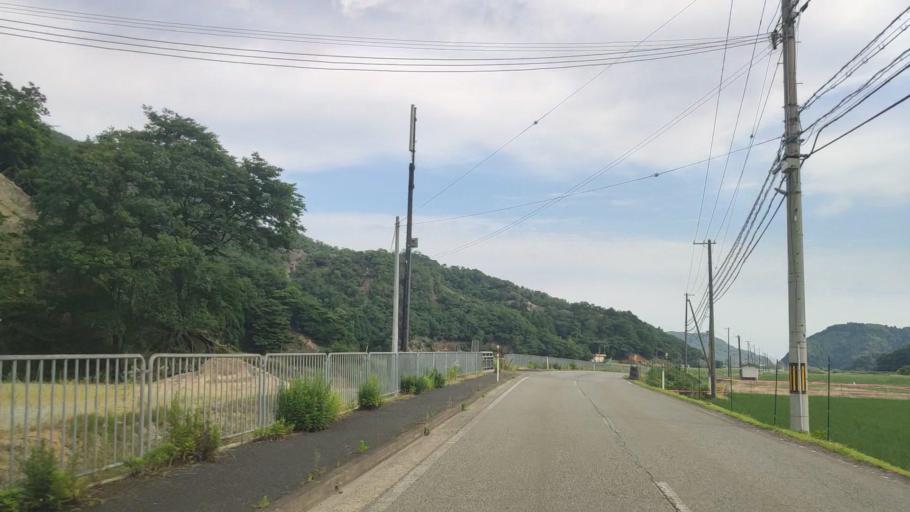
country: JP
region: Hyogo
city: Toyooka
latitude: 35.6206
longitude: 134.8416
